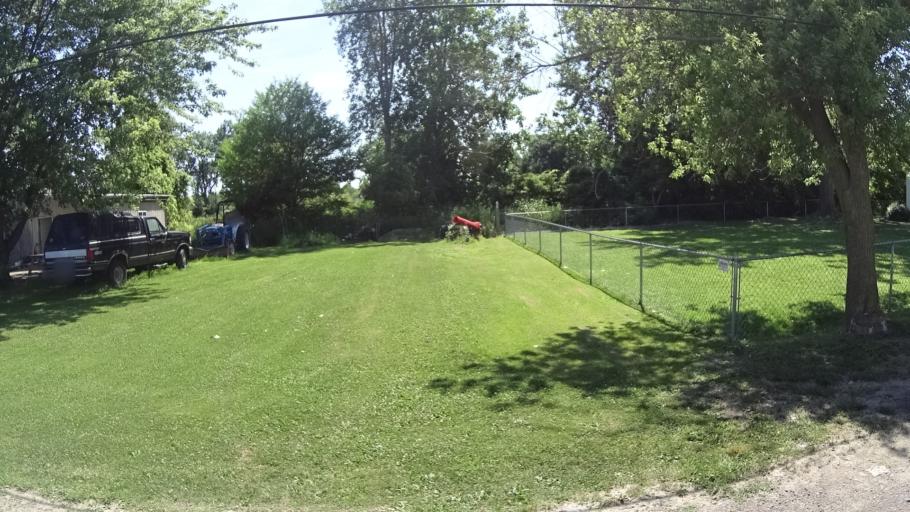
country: US
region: Ohio
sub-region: Ottawa County
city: Port Clinton
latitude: 41.4329
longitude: -82.8961
